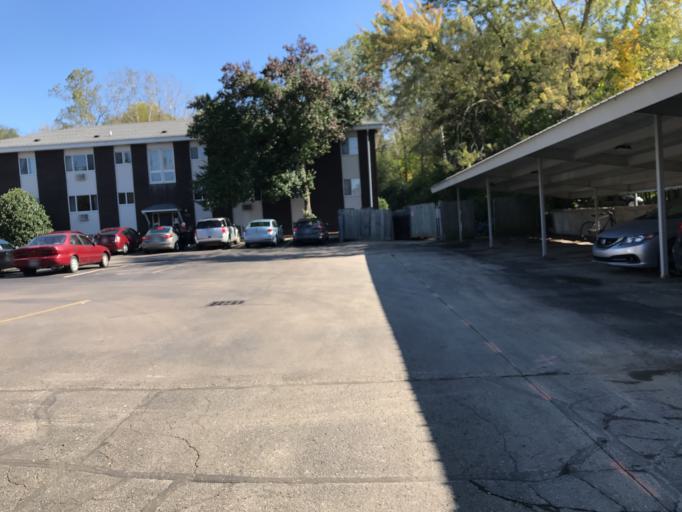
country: US
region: Michigan
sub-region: Washtenaw County
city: Ann Arbor
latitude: 42.2581
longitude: -83.6941
